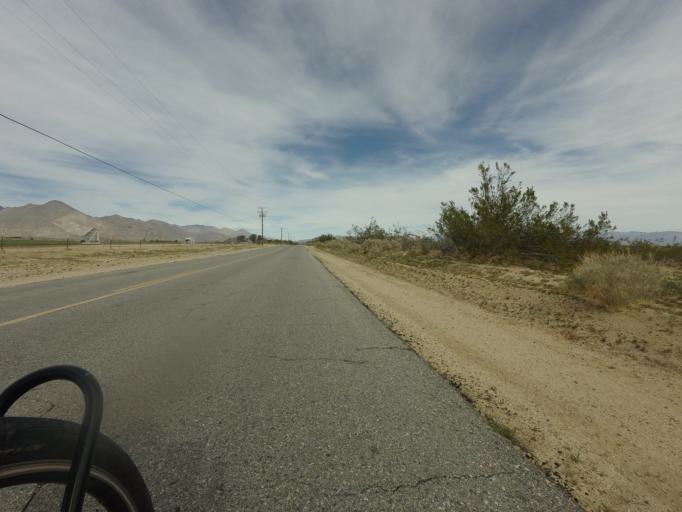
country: US
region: California
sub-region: Kern County
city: Inyokern
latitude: 35.7426
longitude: -117.8407
